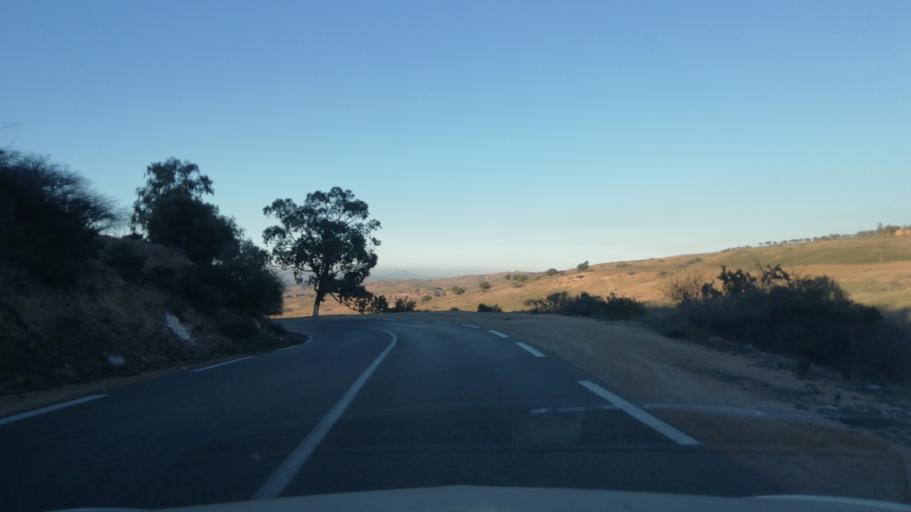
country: DZ
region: Tlemcen
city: Beni Mester
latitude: 34.8210
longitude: -1.6366
